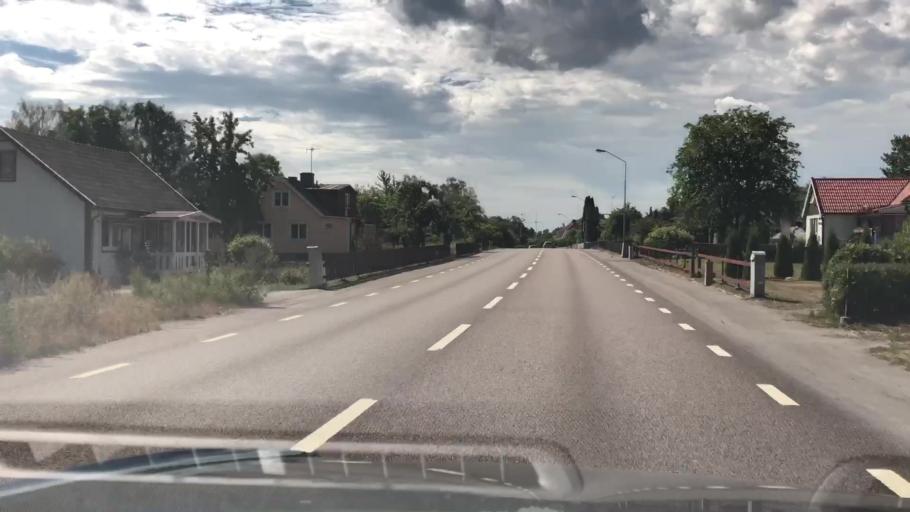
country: SE
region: Kalmar
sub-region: Torsas Kommun
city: Torsas
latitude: 56.3994
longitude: 16.0681
